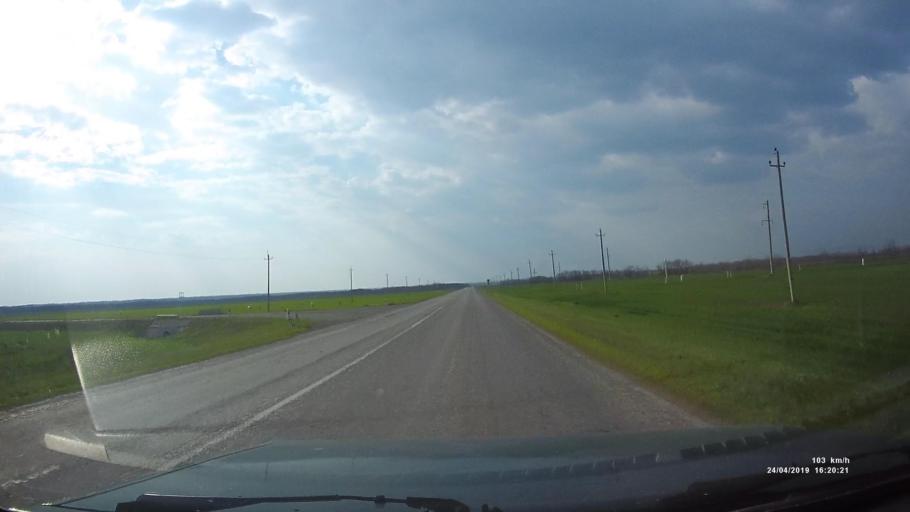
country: RU
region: Rostov
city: Orlovskiy
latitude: 46.7919
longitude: 42.0811
